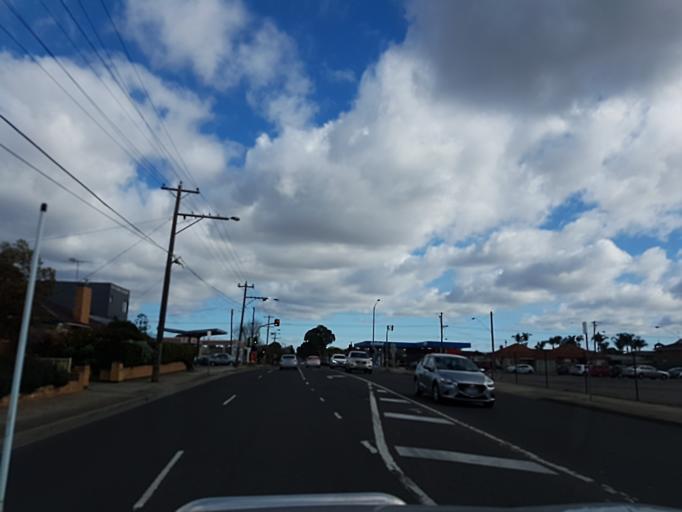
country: AU
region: Victoria
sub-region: Darebin
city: Fairfield
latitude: -37.7656
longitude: 145.0214
